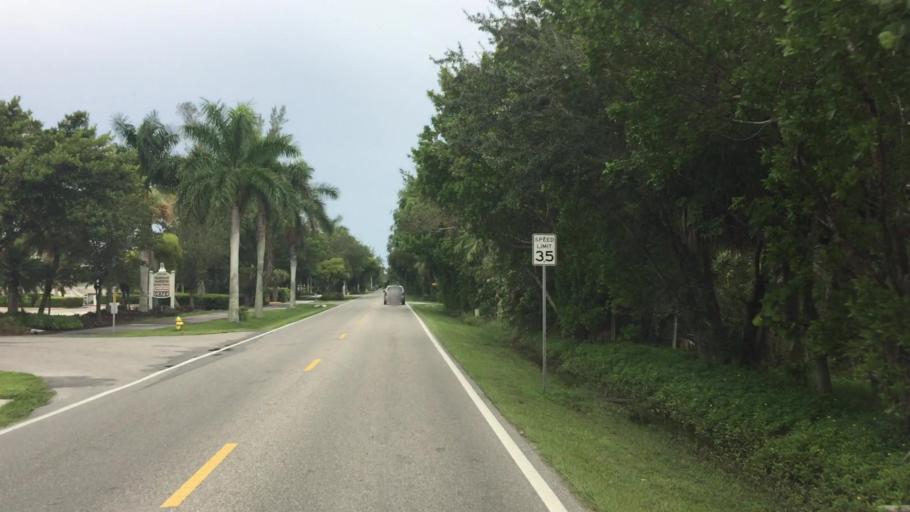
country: US
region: Florida
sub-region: Lee County
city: Sanibel
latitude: 26.4395
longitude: -82.0658
